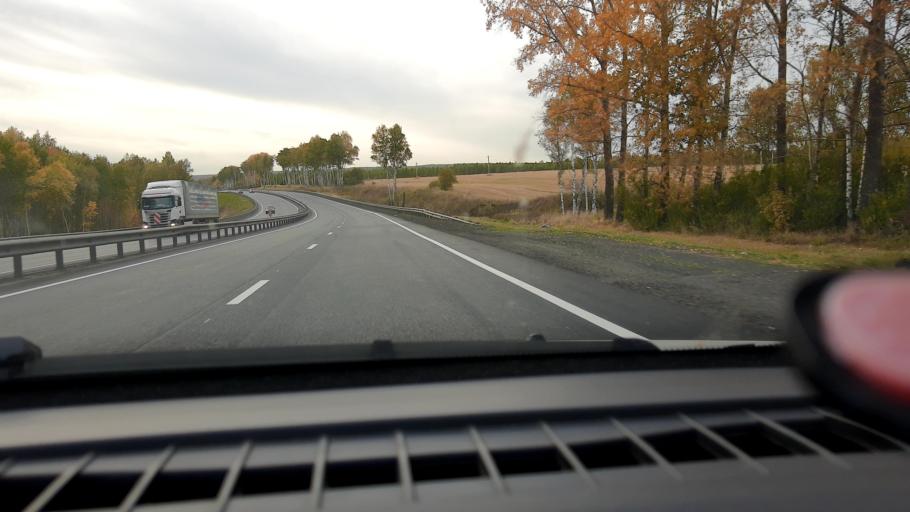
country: RU
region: Vladimir
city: Gorokhovets
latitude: 56.1643
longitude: 42.4934
